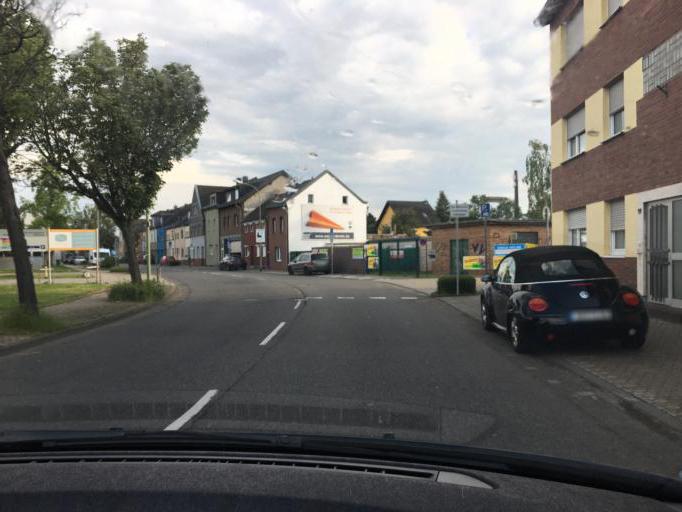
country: DE
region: North Rhine-Westphalia
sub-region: Regierungsbezirk Koln
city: Dueren
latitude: 50.8294
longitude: 6.4566
